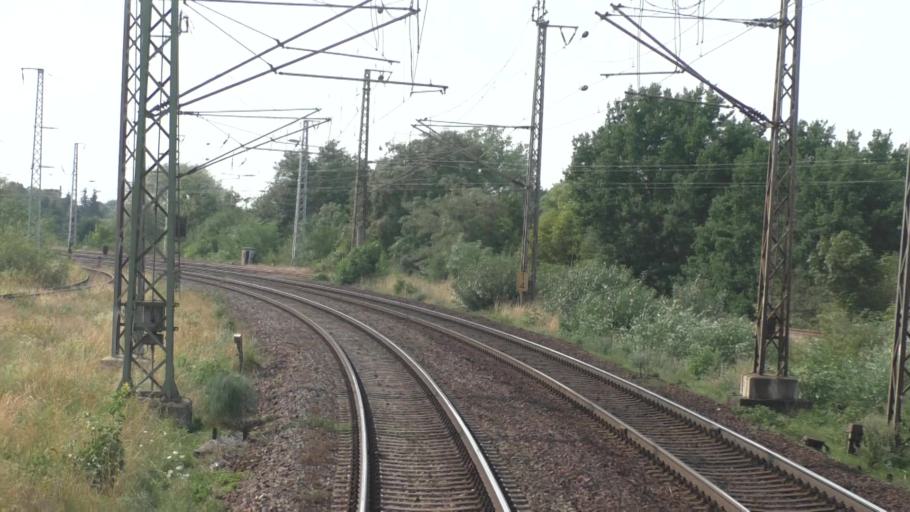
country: DE
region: Saxony-Anhalt
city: Biederitz
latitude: 52.1543
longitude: 11.7275
